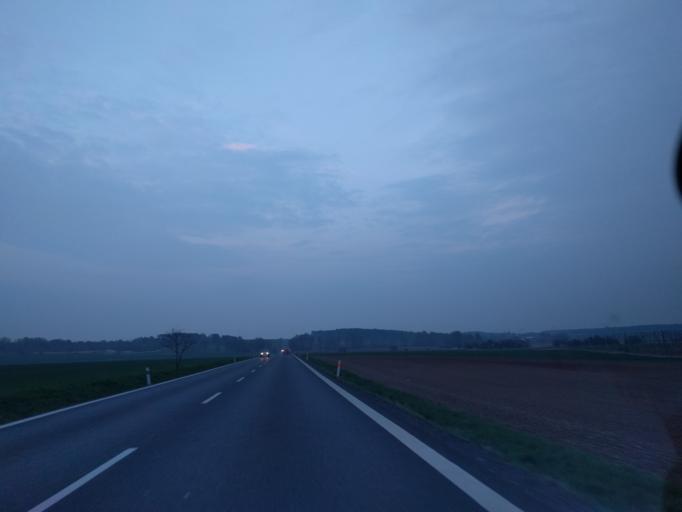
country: CZ
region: Central Bohemia
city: Rakovnik
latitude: 50.1682
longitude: 13.6522
